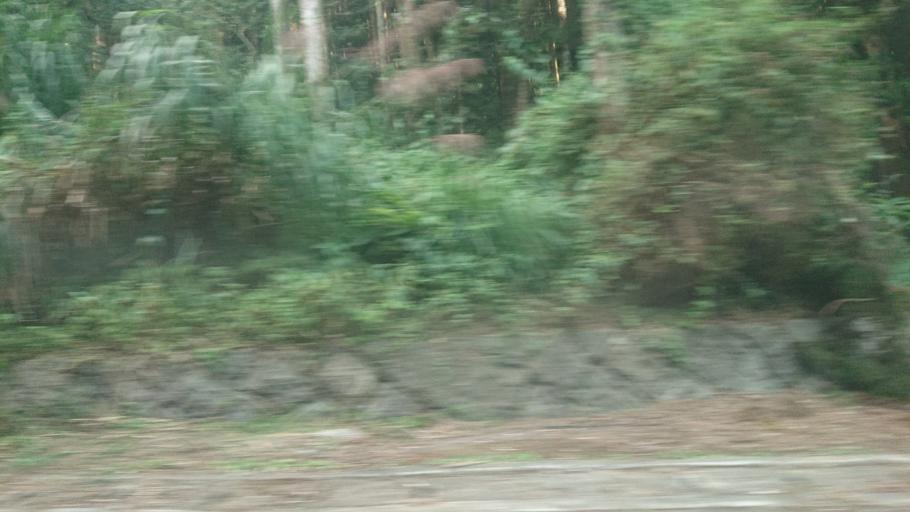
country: TW
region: Taiwan
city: Lugu
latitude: 23.4999
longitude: 120.7829
